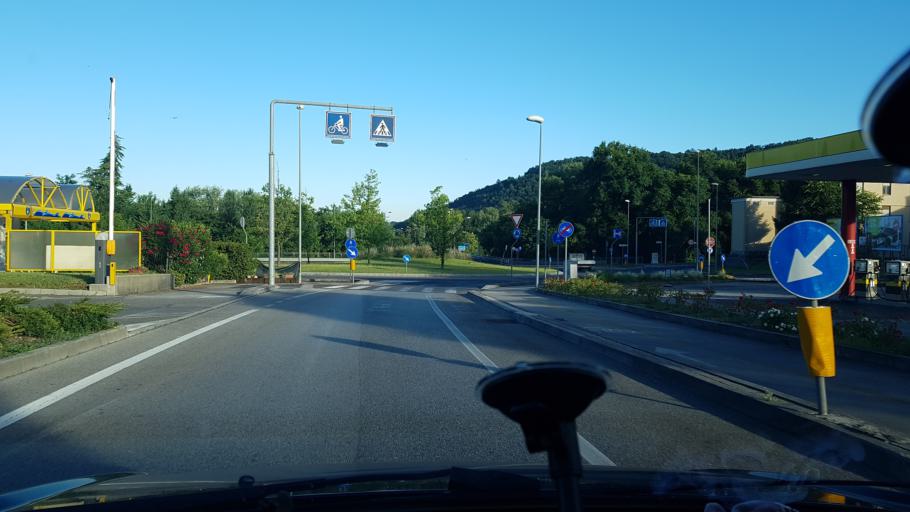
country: IT
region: Friuli Venezia Giulia
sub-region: Provincia di Gorizia
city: Gorizia
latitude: 45.9343
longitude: 13.6014
